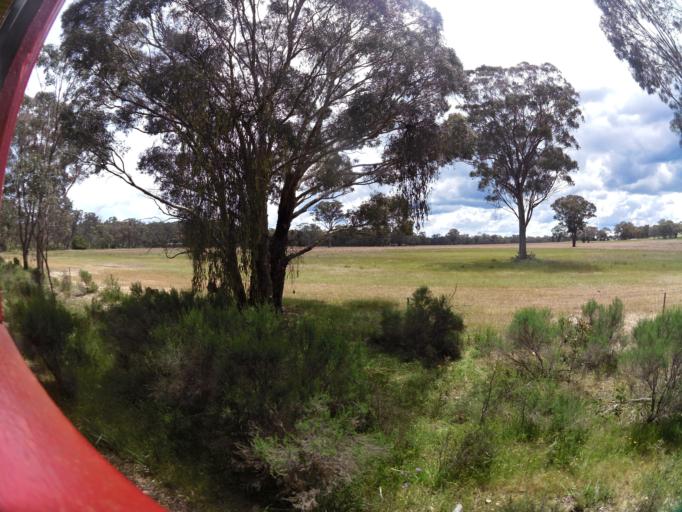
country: AU
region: Victoria
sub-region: Mount Alexander
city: Castlemaine
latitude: -36.9934
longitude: 144.0958
